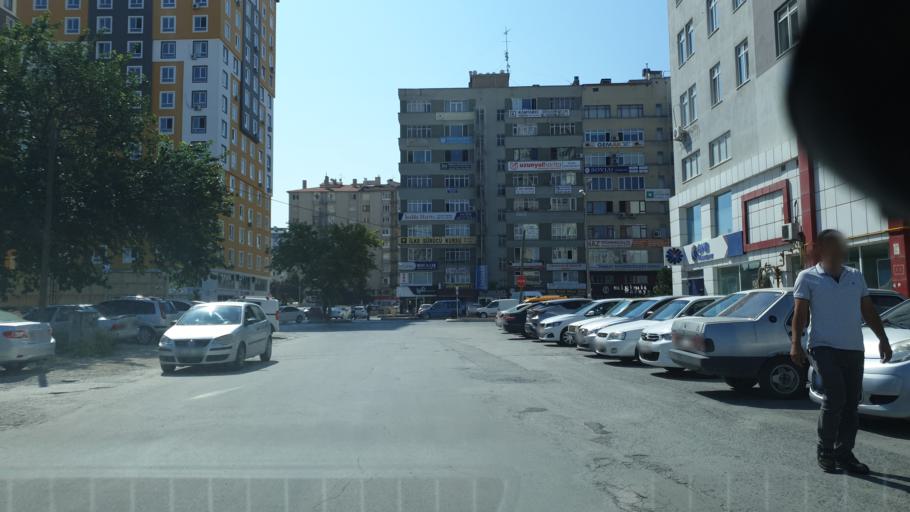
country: TR
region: Kayseri
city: Kayseri
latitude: 38.7253
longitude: 35.4921
